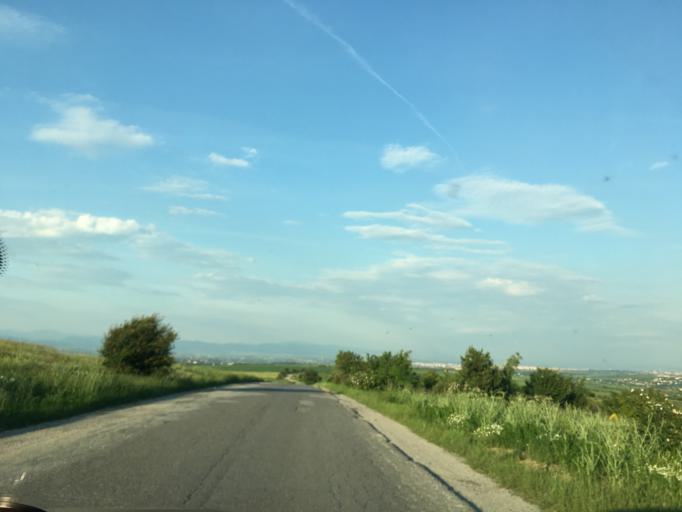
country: BG
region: Sofiya
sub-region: Obshtina Bozhurishte
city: Bozhurishte
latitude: 42.7273
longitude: 23.1119
